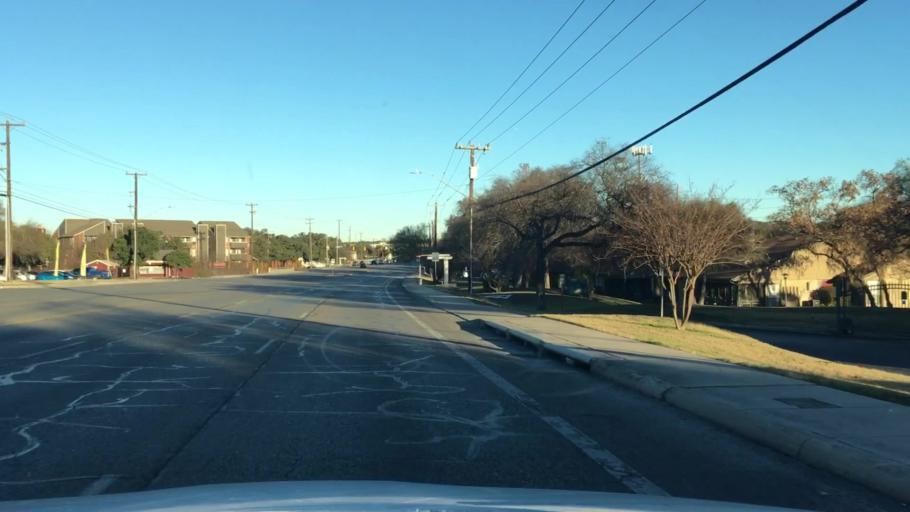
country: US
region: Texas
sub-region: Bexar County
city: Castle Hills
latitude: 29.5533
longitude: -98.5138
